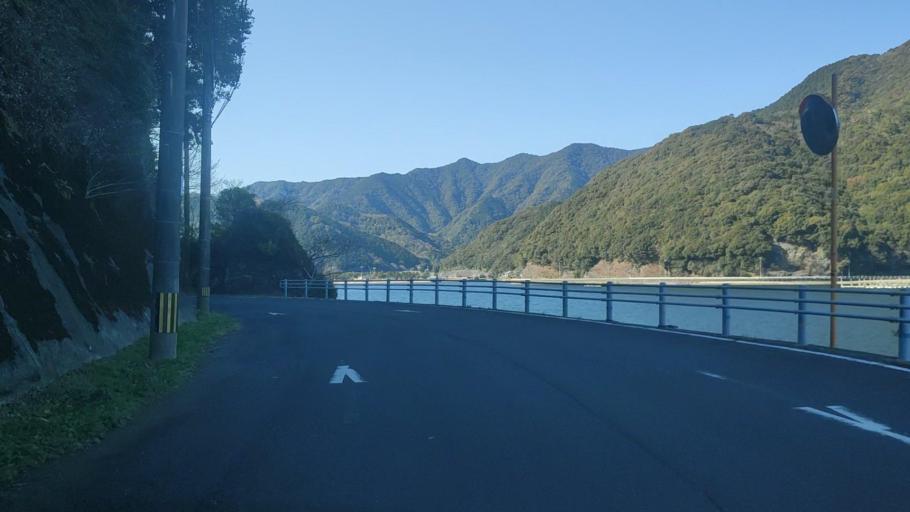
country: JP
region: Oita
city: Saiki
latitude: 32.8365
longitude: 131.9537
